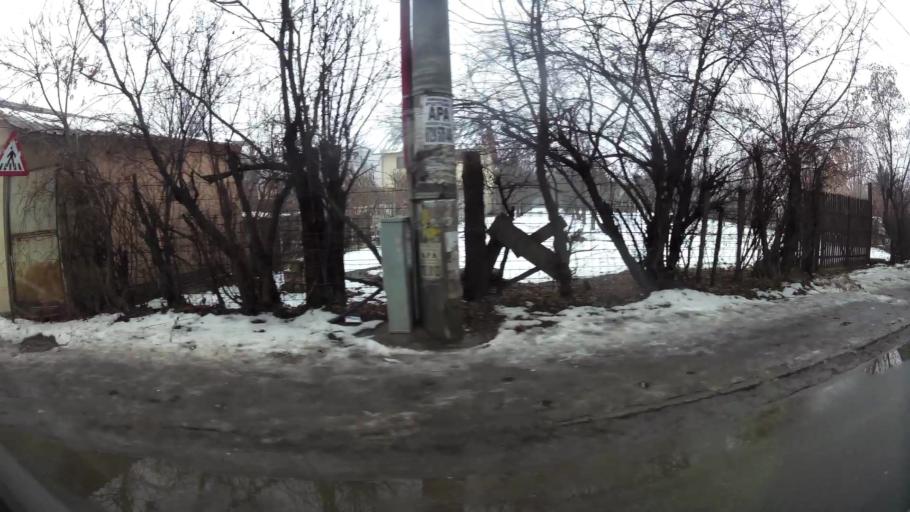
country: RO
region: Ilfov
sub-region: Comuna Chiajna
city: Rosu
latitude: 44.4531
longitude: 25.9951
